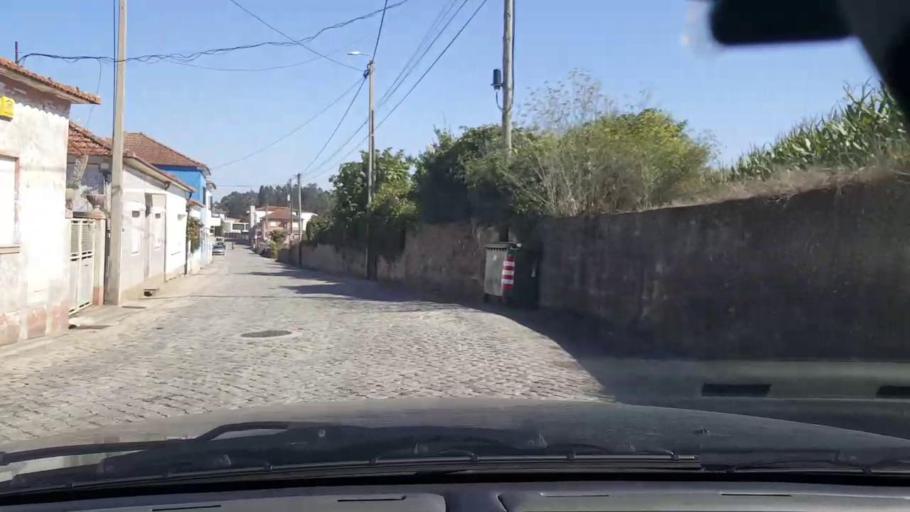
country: PT
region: Porto
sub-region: Matosinhos
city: Lavra
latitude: 41.2947
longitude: -8.6945
